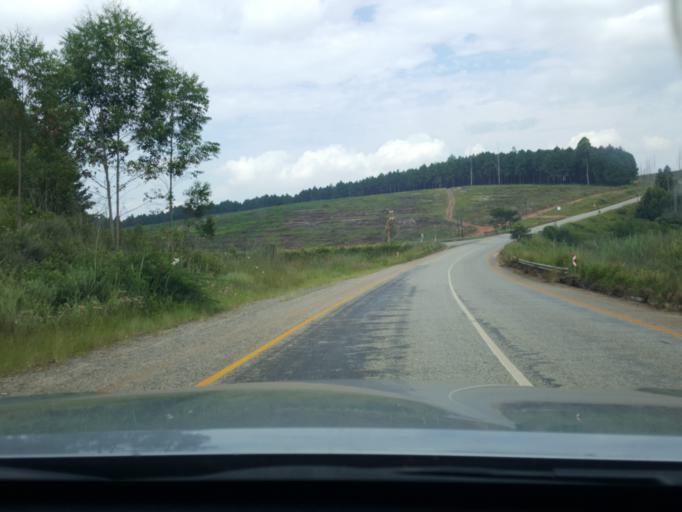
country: ZA
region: Mpumalanga
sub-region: Ehlanzeni District
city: White River
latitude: -25.1943
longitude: 30.9235
